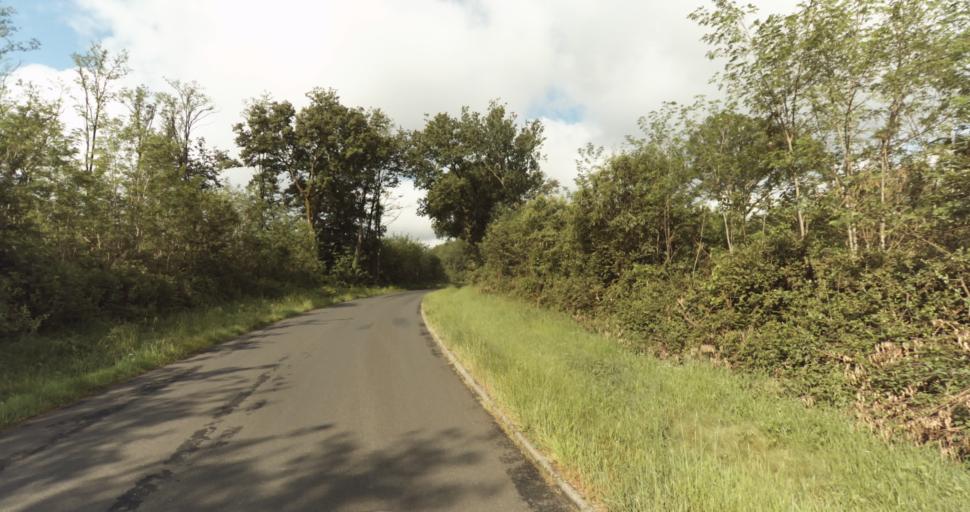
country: FR
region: Aquitaine
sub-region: Departement de la Dordogne
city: Lalinde
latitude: 44.9018
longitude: 0.7741
